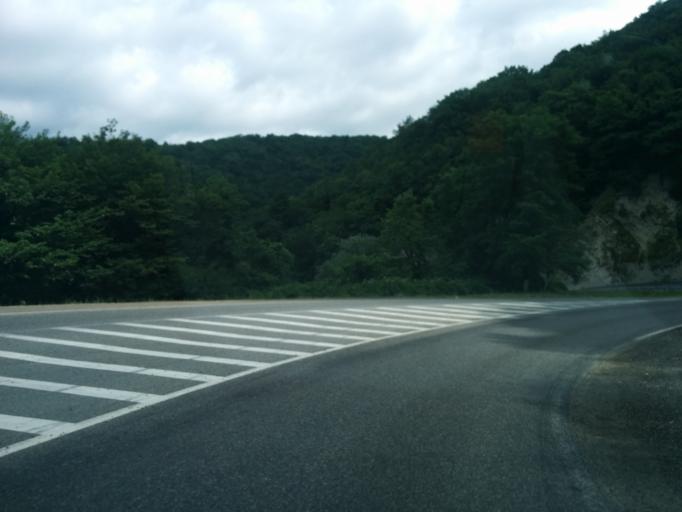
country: RU
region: Krasnodarskiy
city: Agoy
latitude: 44.1424
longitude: 39.0557
